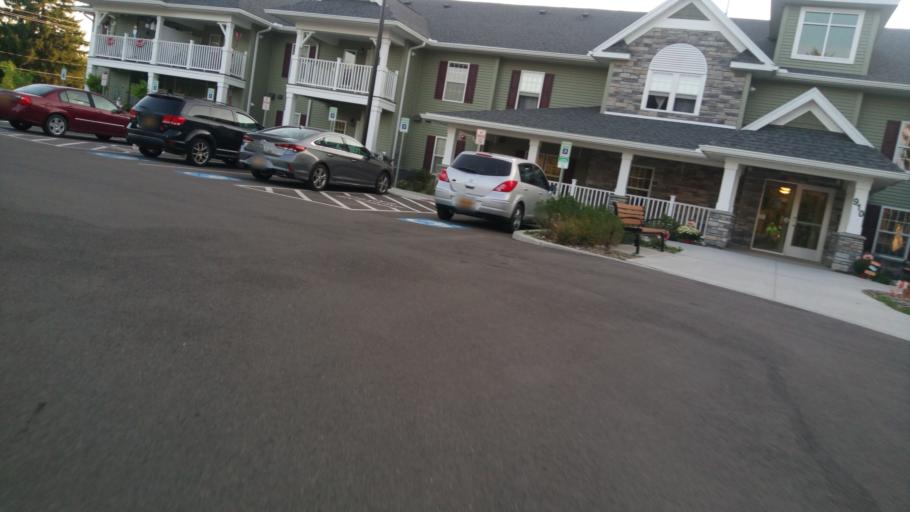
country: US
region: New York
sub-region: Chemung County
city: Elmira
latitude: 42.0740
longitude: -76.7890
